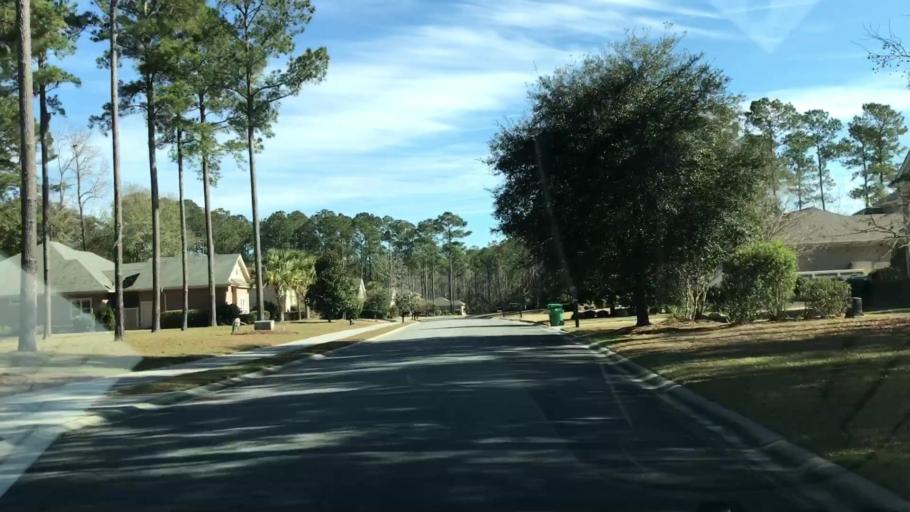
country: US
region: South Carolina
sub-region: Beaufort County
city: Bluffton
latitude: 32.2527
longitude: -80.9200
